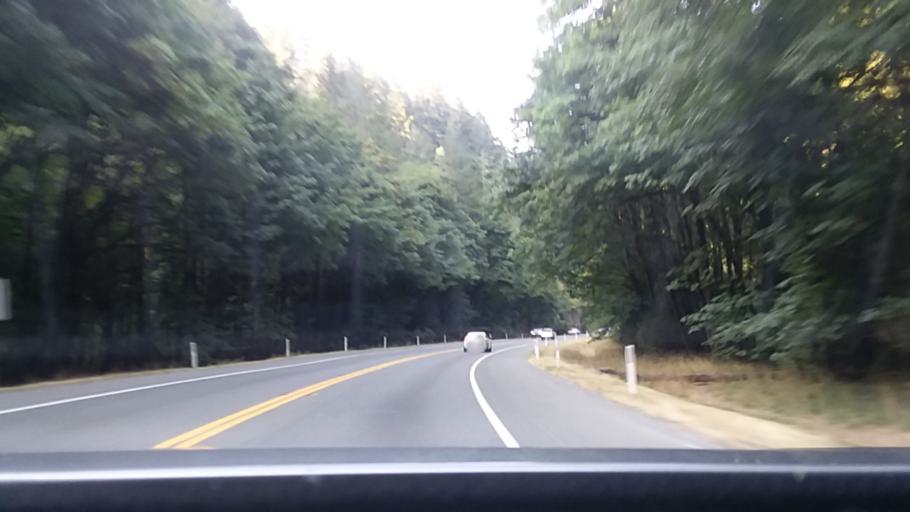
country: CA
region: British Columbia
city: Langford
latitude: 48.4714
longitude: -123.5519
